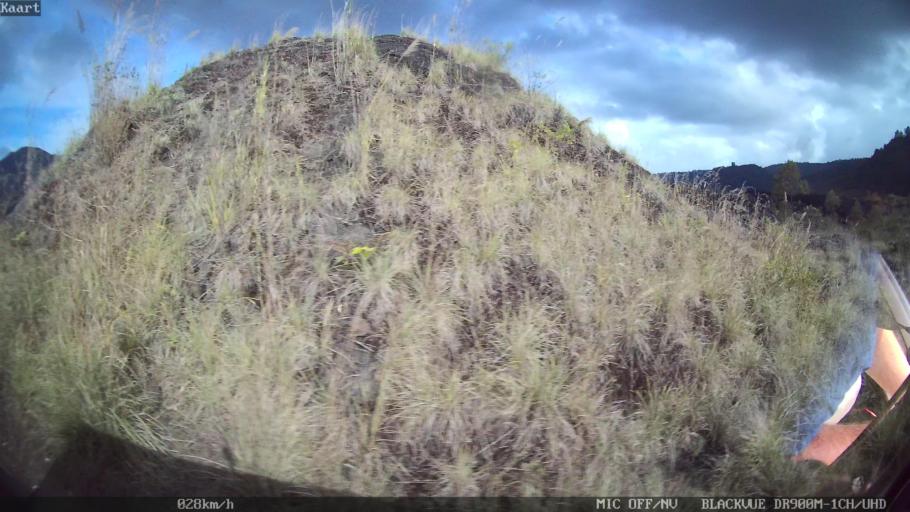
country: ID
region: Bali
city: Banjar Kedisan
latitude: -8.2432
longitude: 115.3507
